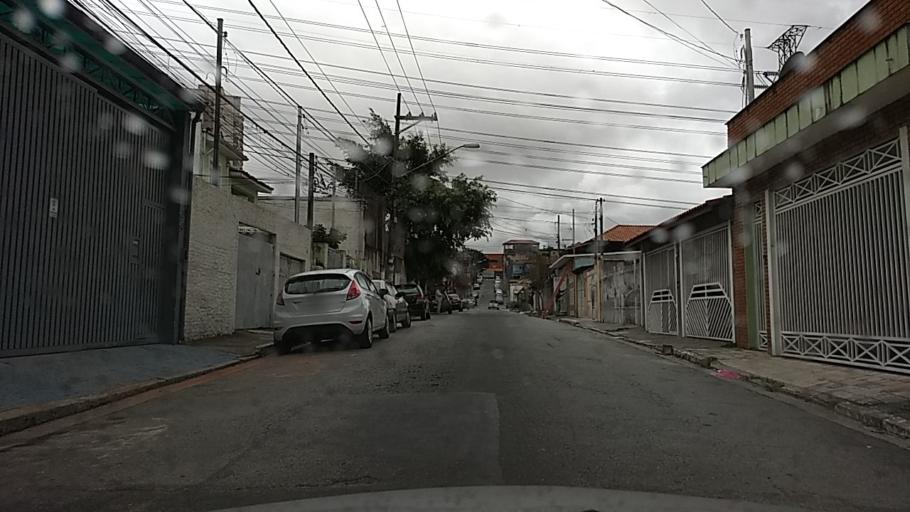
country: BR
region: Sao Paulo
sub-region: Sao Paulo
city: Sao Paulo
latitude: -23.5002
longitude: -46.5961
